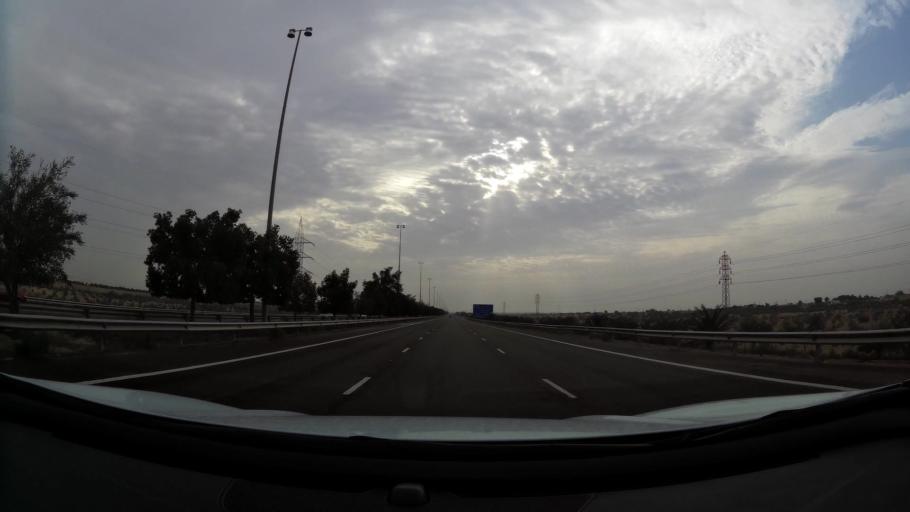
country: AE
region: Abu Dhabi
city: Abu Dhabi
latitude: 24.2030
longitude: 54.9039
